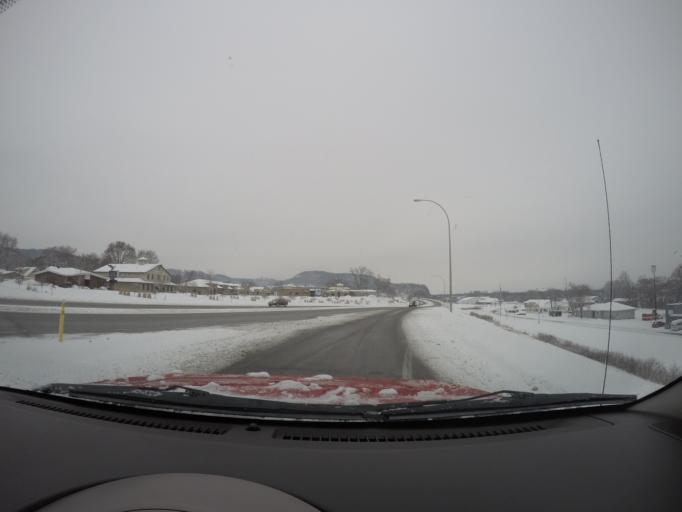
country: US
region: Minnesota
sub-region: Houston County
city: La Crescent
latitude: 43.8262
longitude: -91.3033
